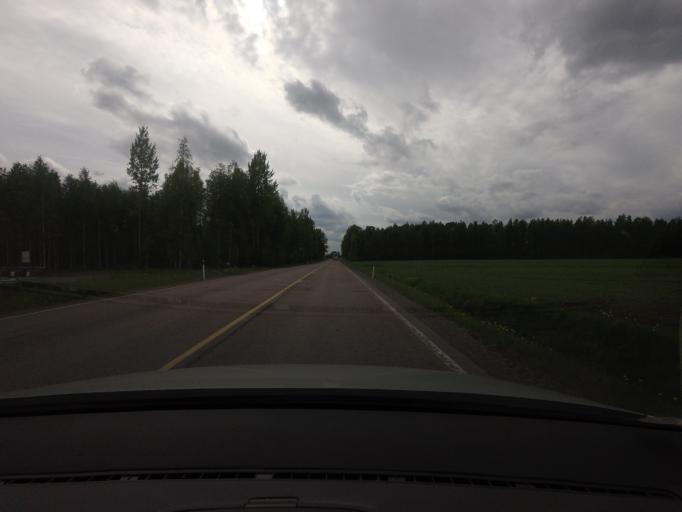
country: FI
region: South Karelia
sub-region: Lappeenranta
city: Taavetti
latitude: 60.9084
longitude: 27.5636
